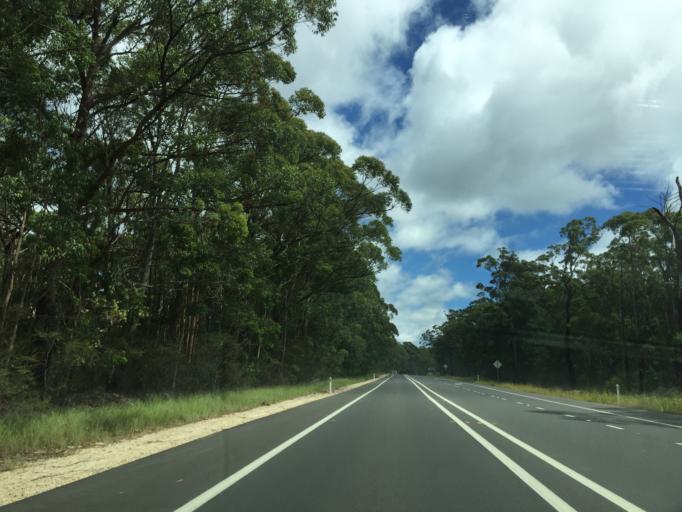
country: AU
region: New South Wales
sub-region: Hawkesbury
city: Richmond
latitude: -33.5132
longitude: 150.5735
